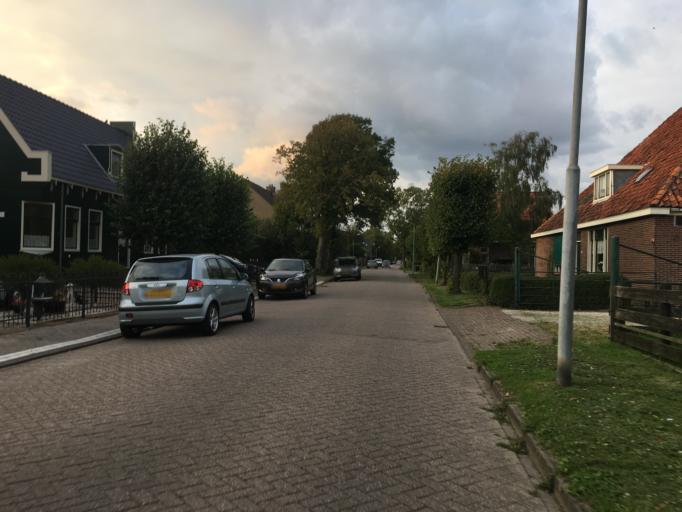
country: NL
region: North Holland
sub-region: Gemeente Zaanstad
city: Zaanstad
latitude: 52.4449
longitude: 4.7773
